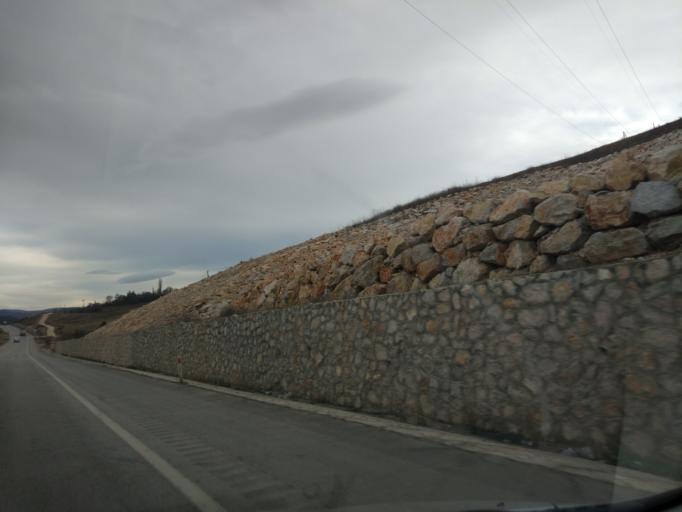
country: TR
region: Karabuk
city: Eskipazar
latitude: 40.9384
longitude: 32.5669
